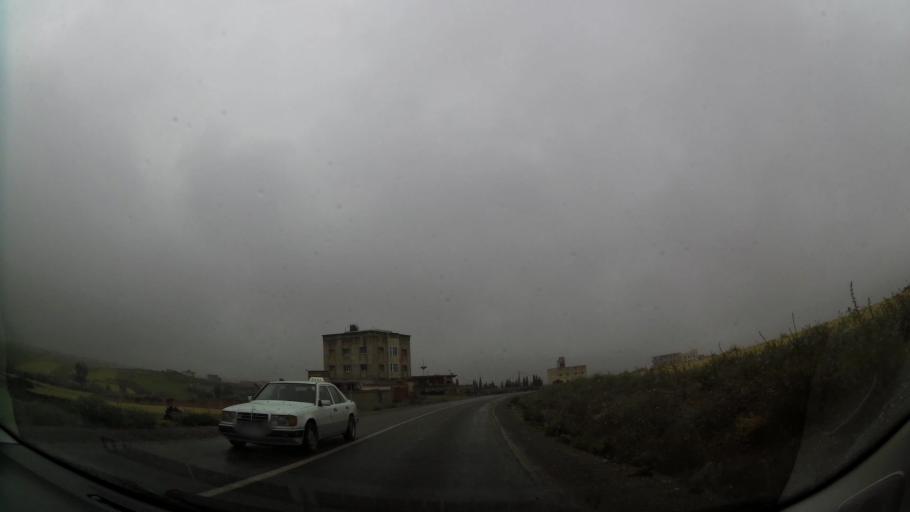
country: MA
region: Oriental
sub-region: Nador
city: Boudinar
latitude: 35.1406
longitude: -3.6128
